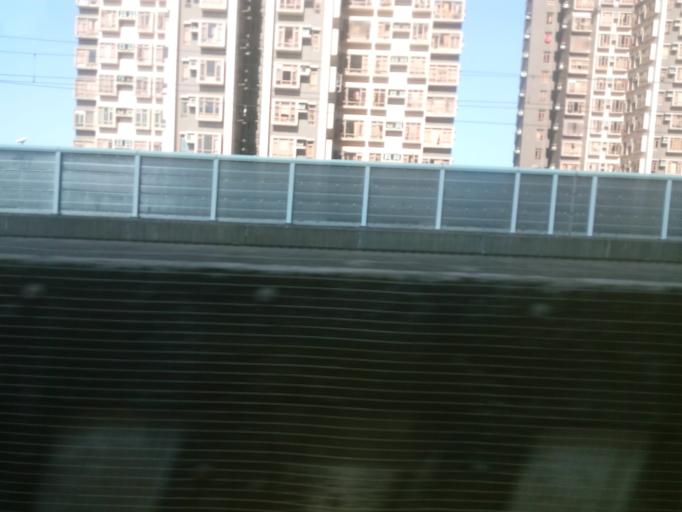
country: HK
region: Sai Kung
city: Sai Kung
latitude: 22.4244
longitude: 114.2299
